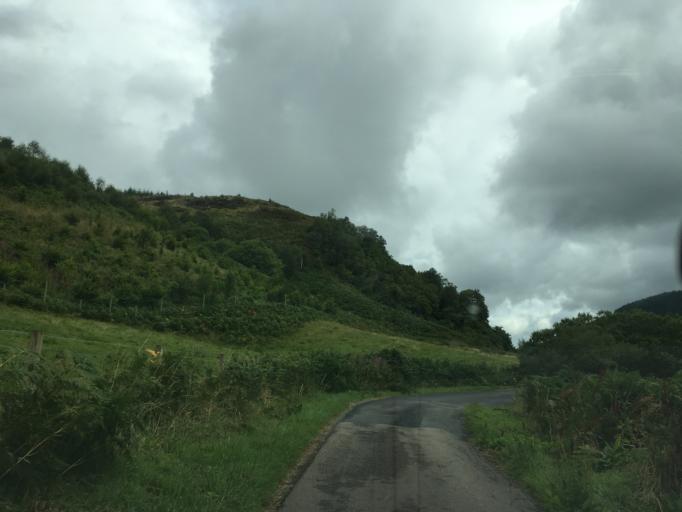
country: GB
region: Scotland
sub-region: Argyll and Bute
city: Oban
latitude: 56.2592
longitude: -5.3975
